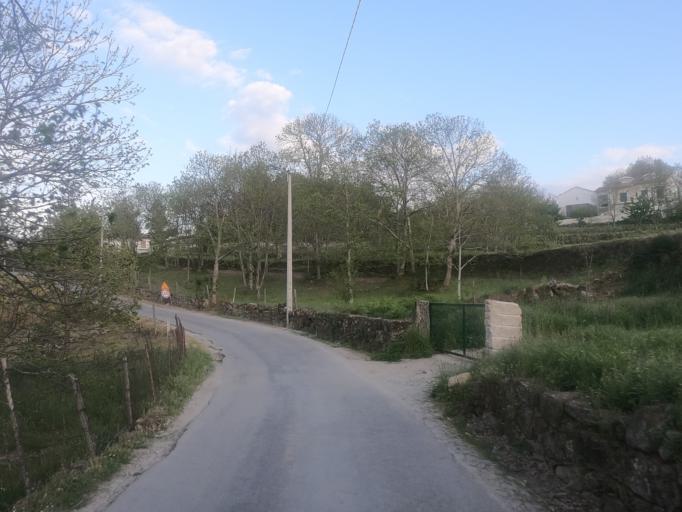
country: PT
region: Vila Real
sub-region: Santa Marta de Penaguiao
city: Santa Marta de Penaguiao
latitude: 41.2760
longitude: -7.8127
